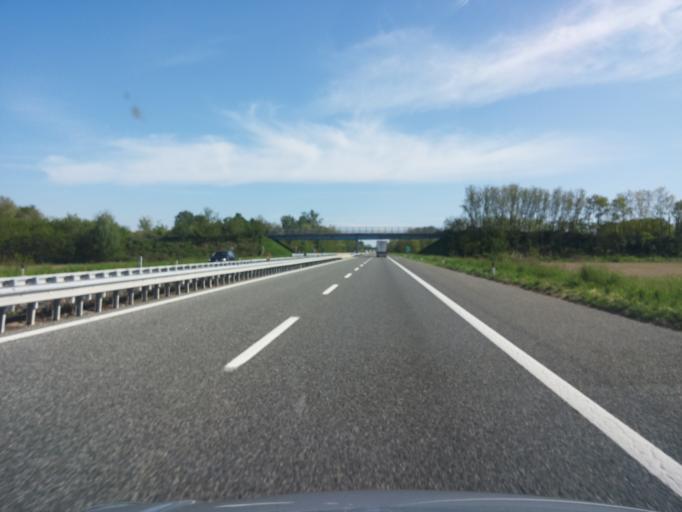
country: IT
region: Piedmont
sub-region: Provincia di Novara
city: Sizzano
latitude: 45.5598
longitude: 8.4175
